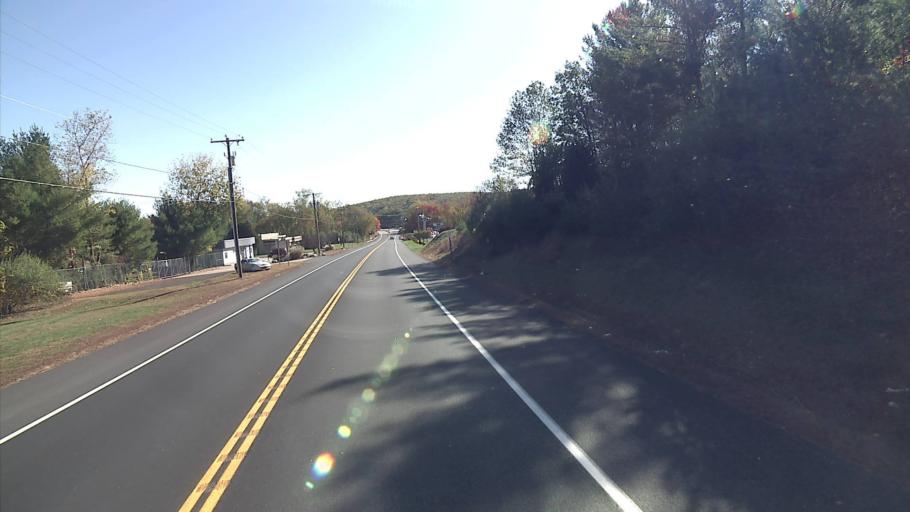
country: US
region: Connecticut
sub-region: Tolland County
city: South Coventry
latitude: 41.7212
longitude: -72.2859
